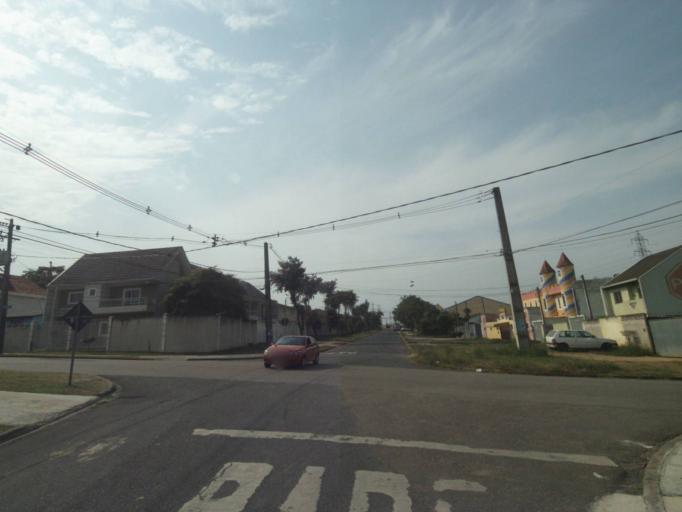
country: BR
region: Parana
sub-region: Pinhais
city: Pinhais
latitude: -25.4853
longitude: -49.2086
